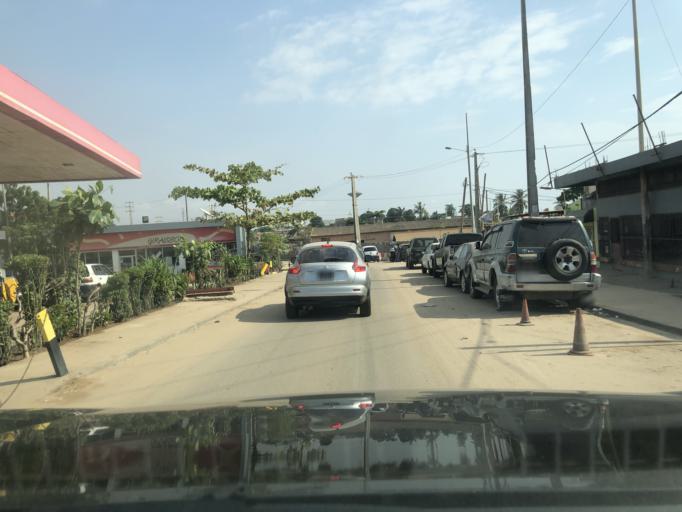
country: AO
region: Luanda
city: Luanda
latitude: -8.8504
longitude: 13.2575
